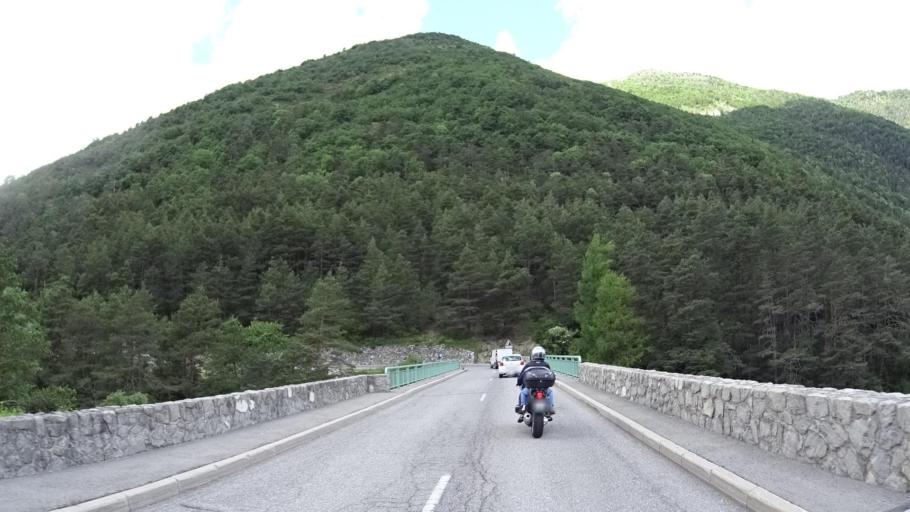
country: FR
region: Provence-Alpes-Cote d'Azur
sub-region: Departement des Alpes-de-Haute-Provence
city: Annot
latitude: 44.0372
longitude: 6.5631
